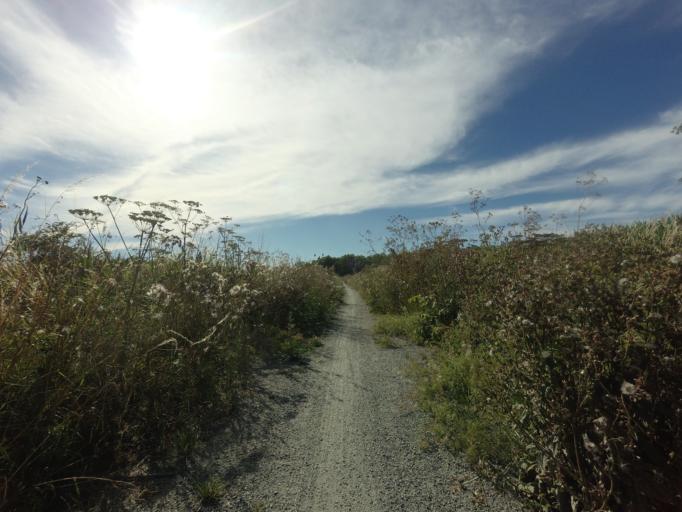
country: GB
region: England
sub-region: Kent
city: Herne Bay
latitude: 51.3650
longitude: 1.2039
